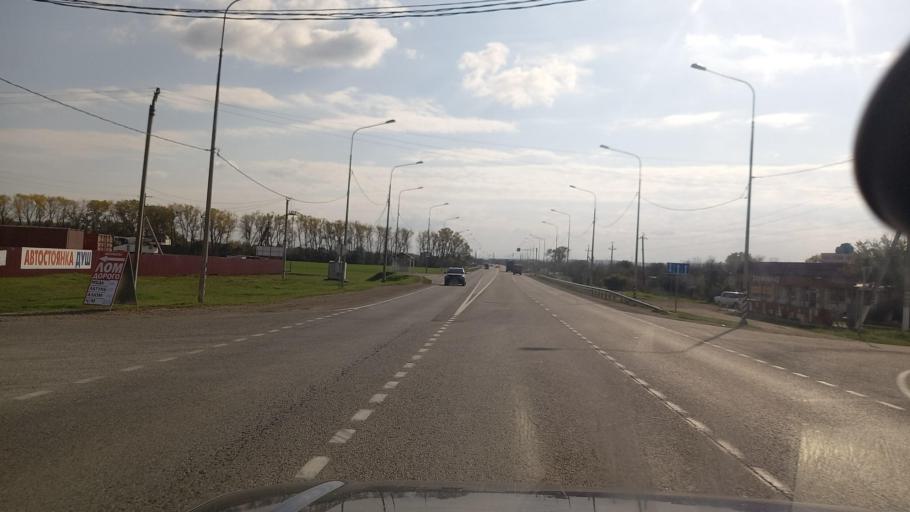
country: RU
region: Krasnodarskiy
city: Novoukrainskiy
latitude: 44.9034
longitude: 38.0328
